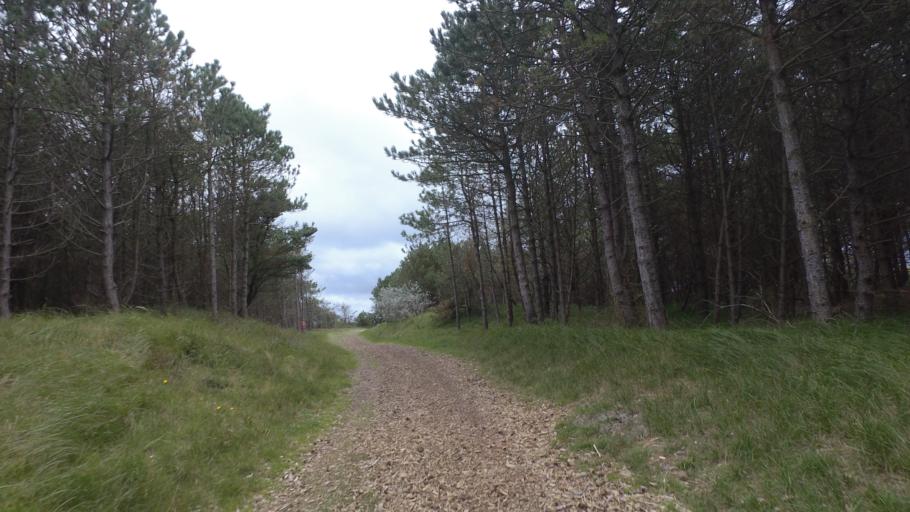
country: NL
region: Friesland
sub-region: Gemeente Ameland
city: Nes
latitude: 53.4583
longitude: 5.7837
